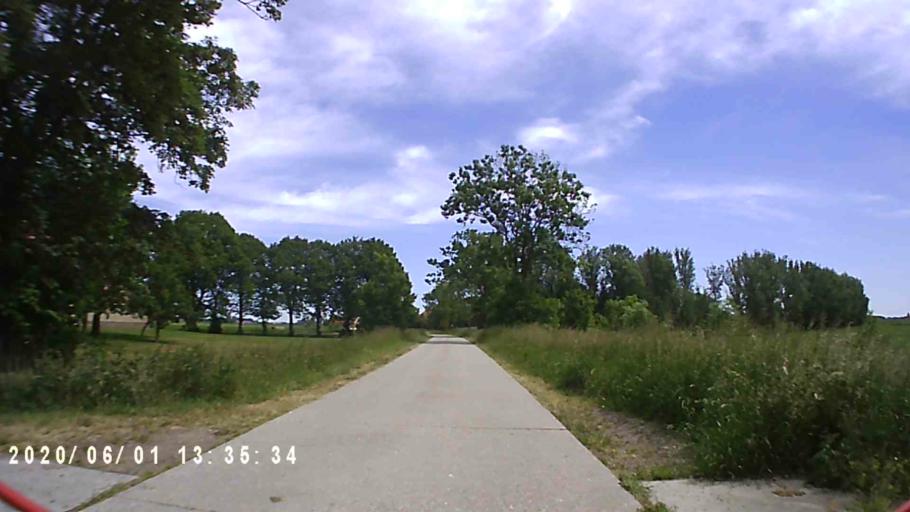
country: NL
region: Friesland
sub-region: Gemeente Littenseradiel
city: Wommels
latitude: 53.0875
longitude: 5.5831
